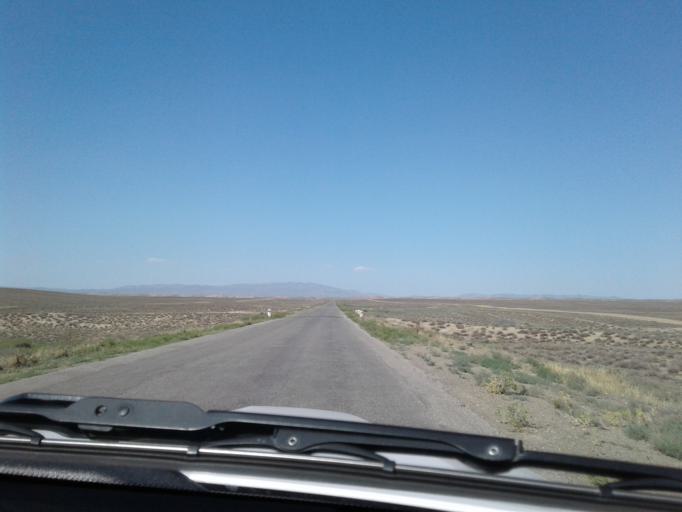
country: TM
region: Balkan
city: Magtymguly
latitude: 38.6089
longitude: 56.2110
